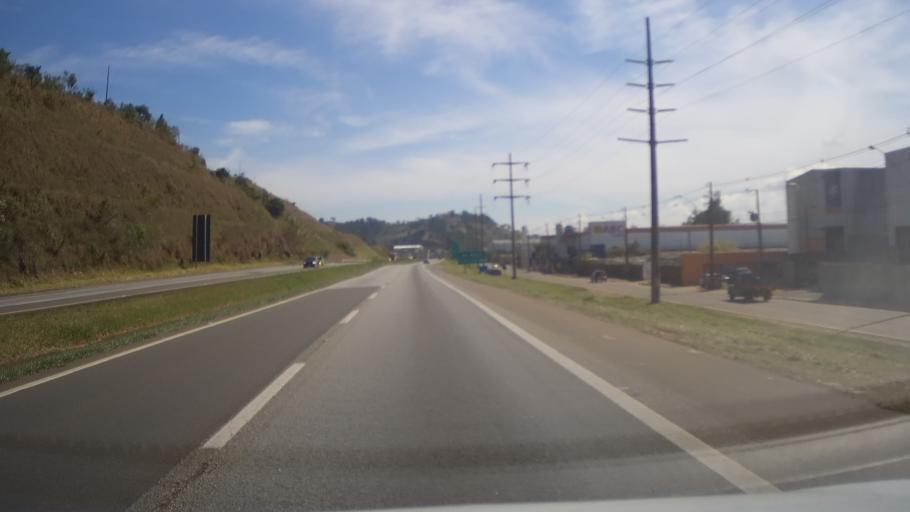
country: BR
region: Minas Gerais
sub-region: Cambui
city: Cambui
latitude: -22.6028
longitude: -46.0586
